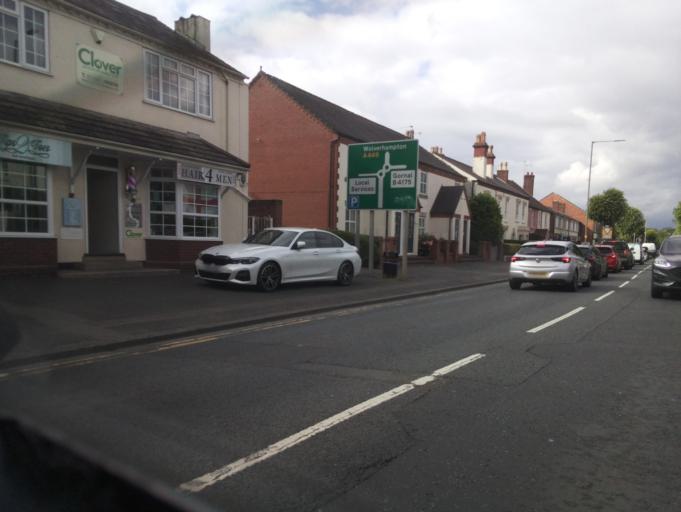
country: GB
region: England
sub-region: Dudley
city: Kingswinford
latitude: 52.5043
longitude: -2.1789
